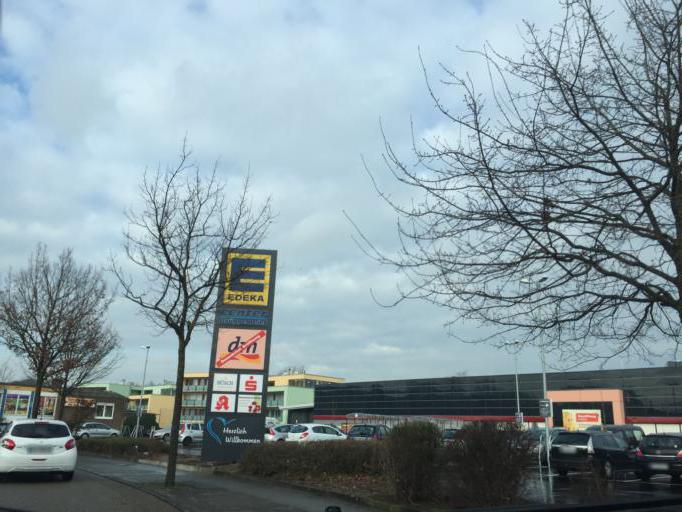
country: DE
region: North Rhine-Westphalia
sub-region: Regierungsbezirk Dusseldorf
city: Kleve
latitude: 51.7921
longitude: 6.1400
